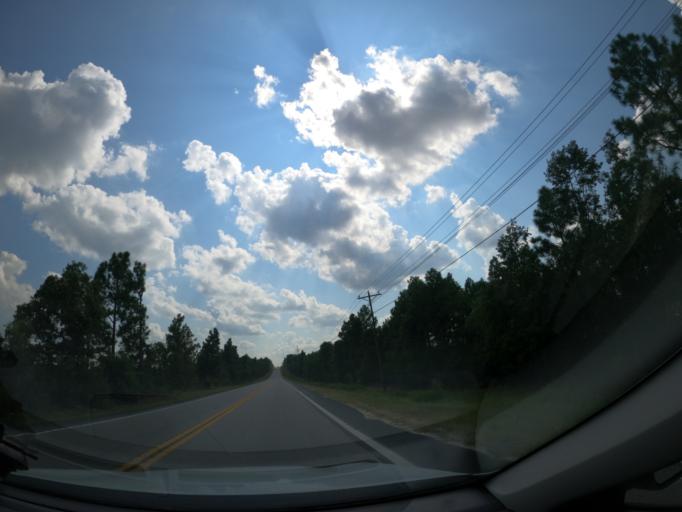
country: US
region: South Carolina
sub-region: Lexington County
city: South Congaree
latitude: 33.8791
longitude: -81.1769
